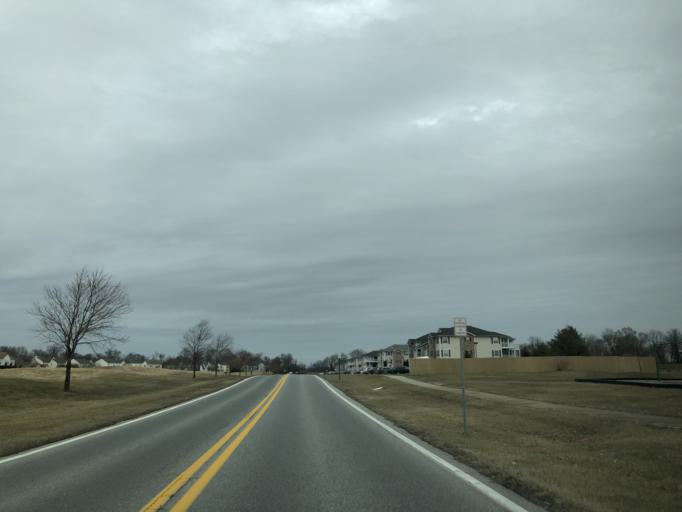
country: US
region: Delaware
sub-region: New Castle County
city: Middletown
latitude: 39.4670
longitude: -75.7110
